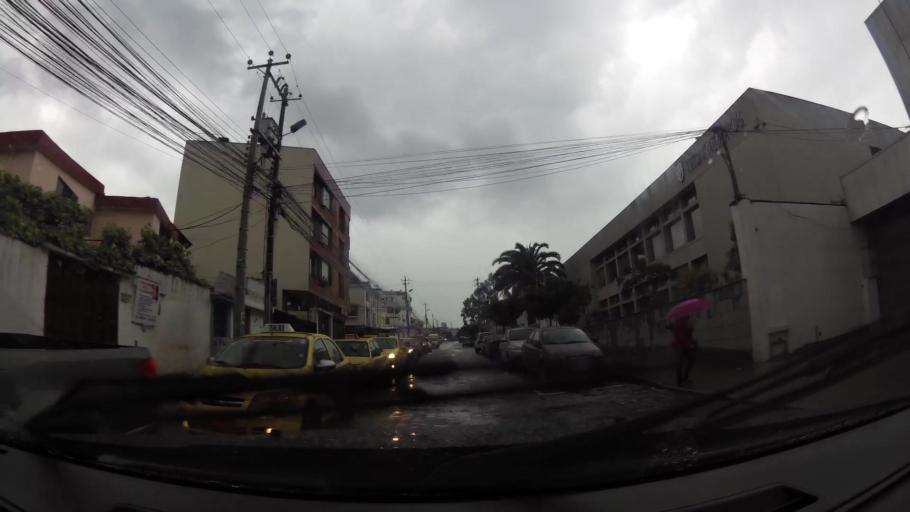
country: EC
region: Pichincha
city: Quito
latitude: -0.1600
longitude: -78.4658
